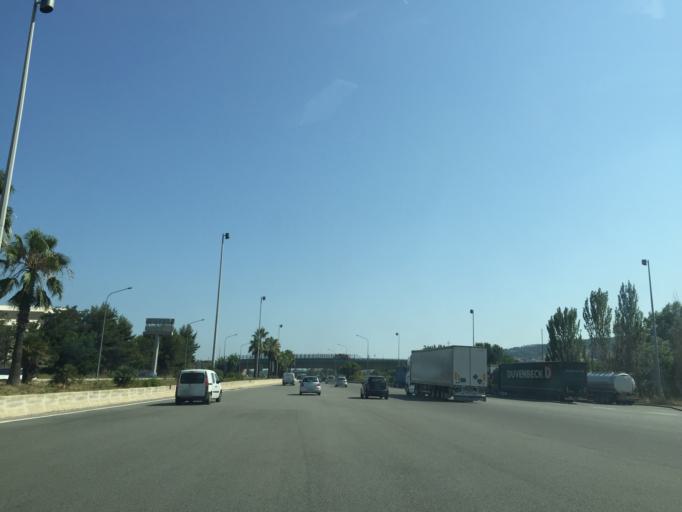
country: FR
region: Provence-Alpes-Cote d'Azur
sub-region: Departement des Alpes-Maritimes
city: Saint-Laurent-du-Var
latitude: 43.6993
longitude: 7.1885
